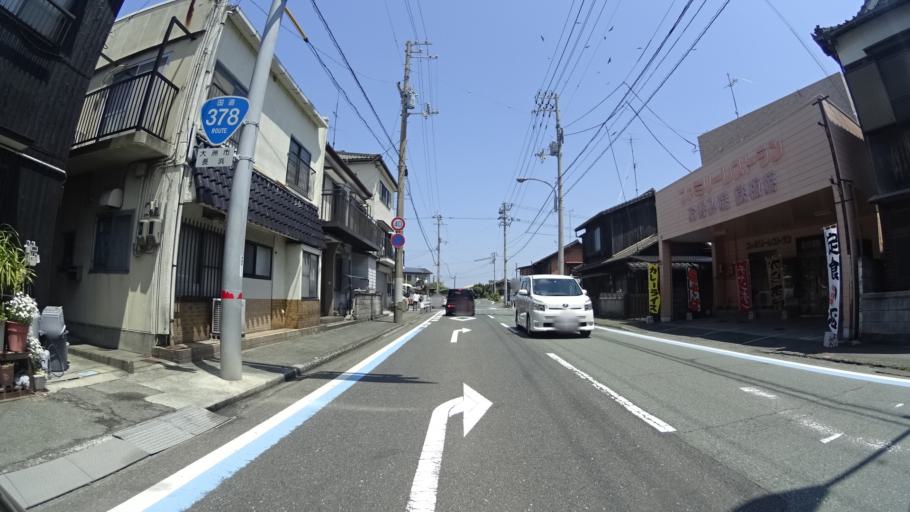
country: JP
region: Ehime
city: Ozu
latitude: 33.6157
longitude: 132.4808
